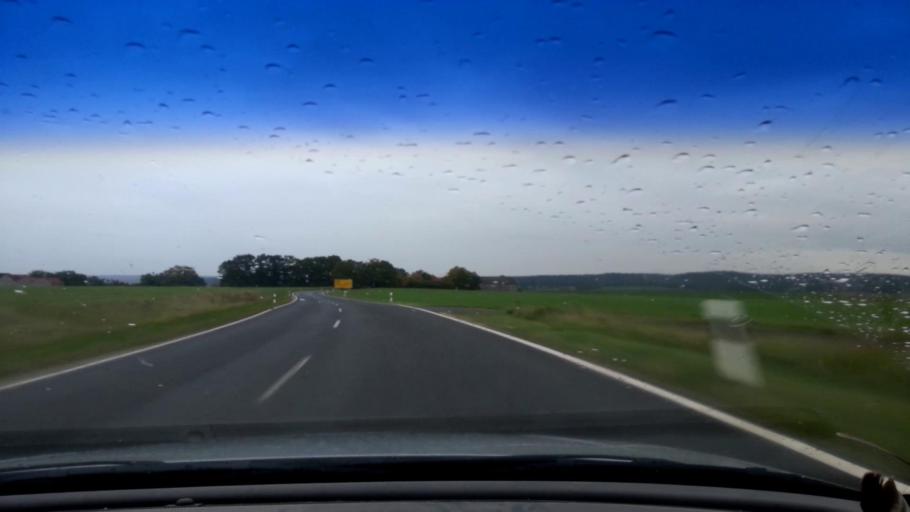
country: DE
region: Bavaria
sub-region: Upper Franconia
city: Priesendorf
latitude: 49.8635
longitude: 10.7176
